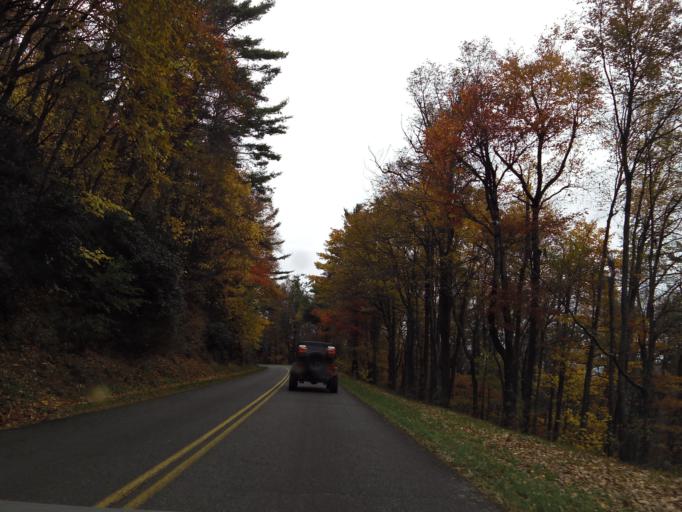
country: US
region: North Carolina
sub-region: Ashe County
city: West Jefferson
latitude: 36.2383
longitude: -81.4945
